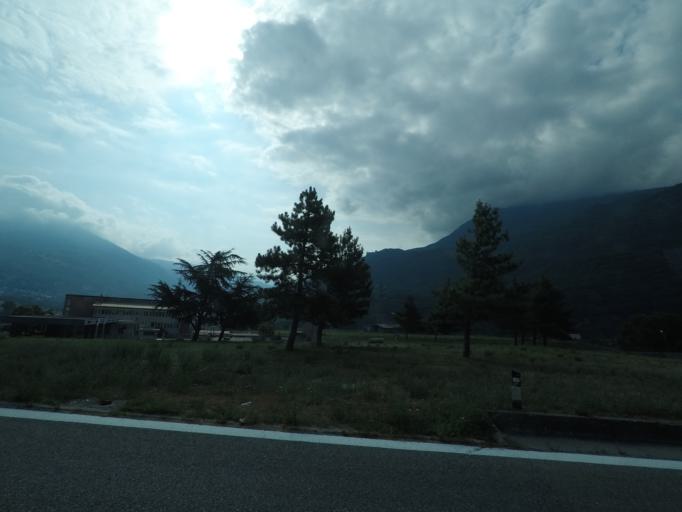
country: IT
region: Aosta Valley
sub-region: Valle d'Aosta
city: Chatillon
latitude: 45.7486
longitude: 7.6188
